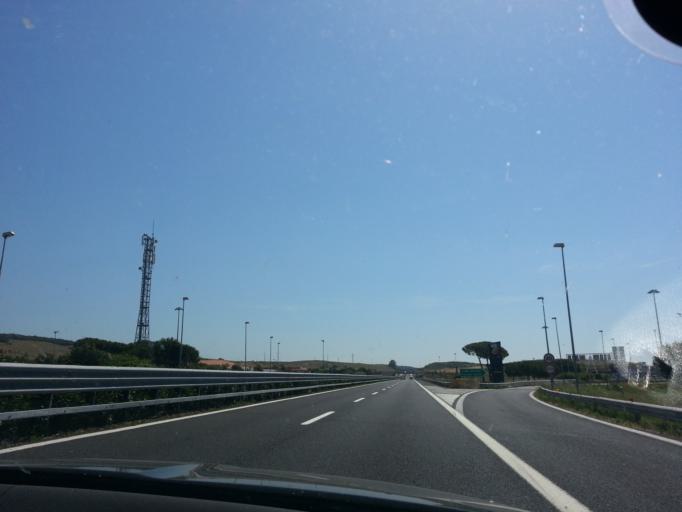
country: IT
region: Latium
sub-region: Citta metropolitana di Roma Capitale
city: Santa Marinella
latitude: 42.0304
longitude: 11.9597
